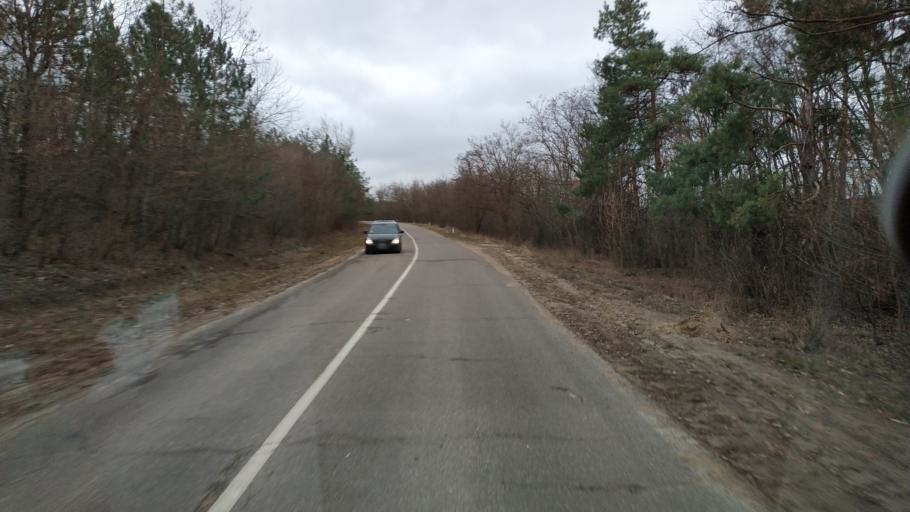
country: MD
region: Calarasi
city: Calarasi
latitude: 47.2324
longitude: 28.2737
